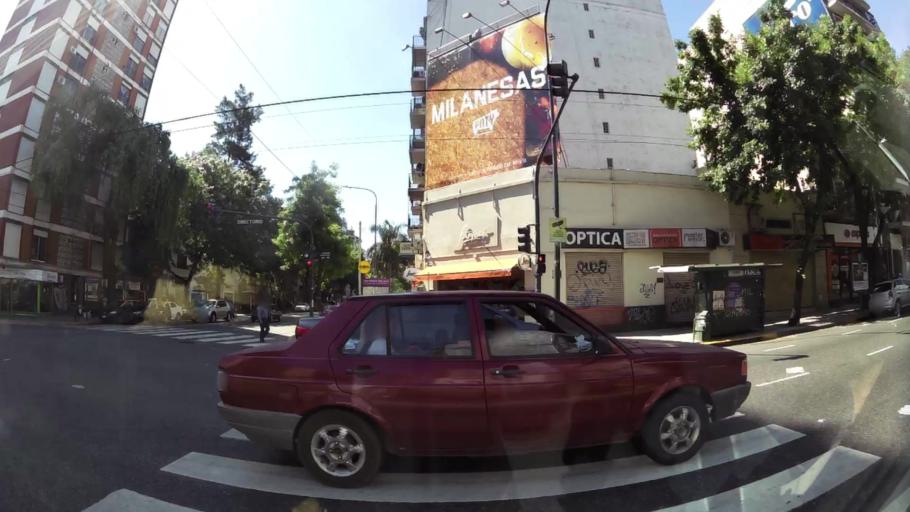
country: AR
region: Buenos Aires F.D.
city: Villa Santa Rita
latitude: -34.6280
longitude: -58.4337
